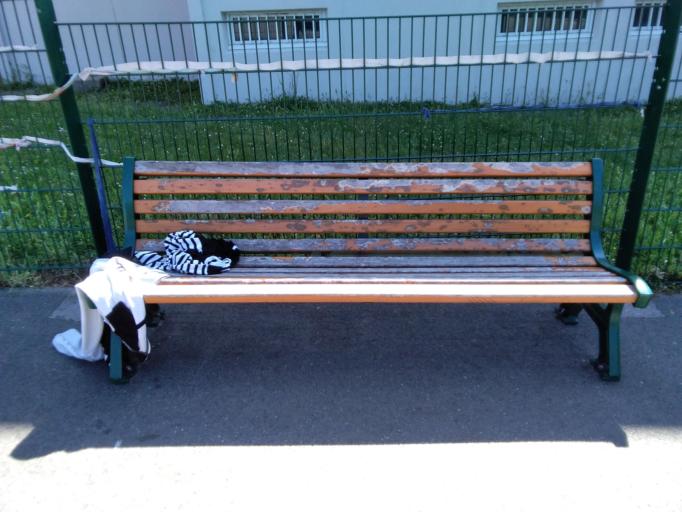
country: FR
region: Picardie
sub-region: Departement de la Somme
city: Rivery
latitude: 49.9106
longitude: 2.3244
